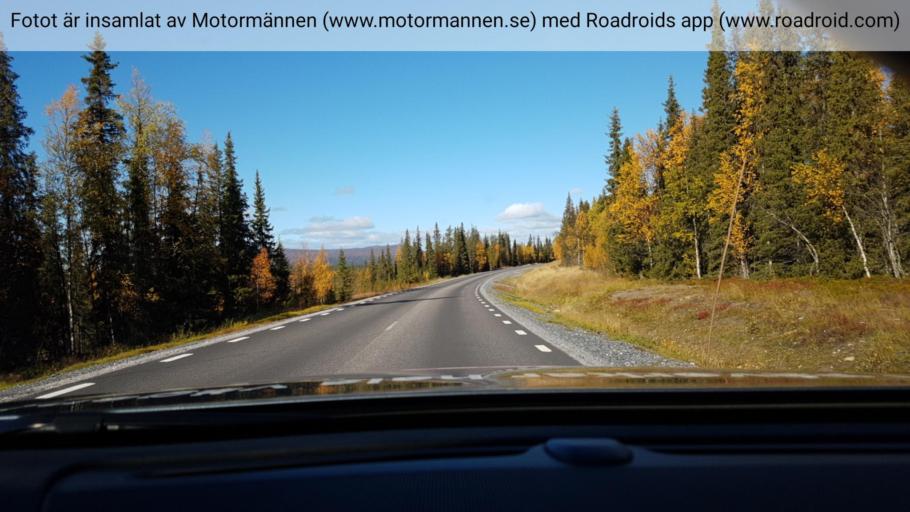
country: SE
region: Norrbotten
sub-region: Gallivare Kommun
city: Gaellivare
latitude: 67.0279
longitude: 20.7298
